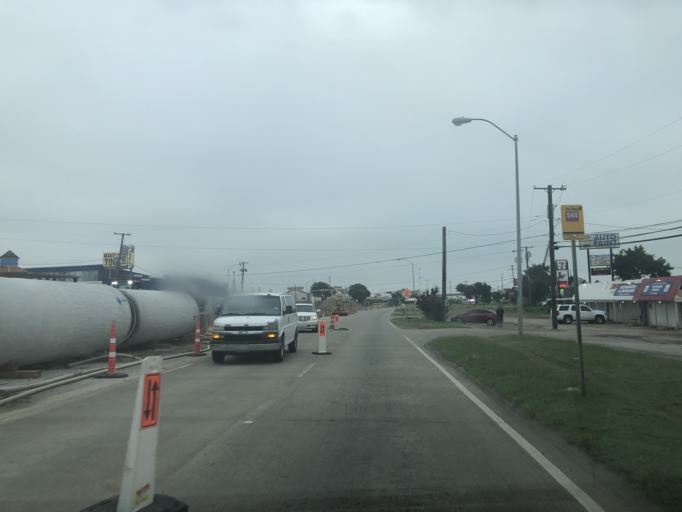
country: US
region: Texas
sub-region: Dallas County
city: Farmers Branch
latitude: 32.8632
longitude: -96.8812
